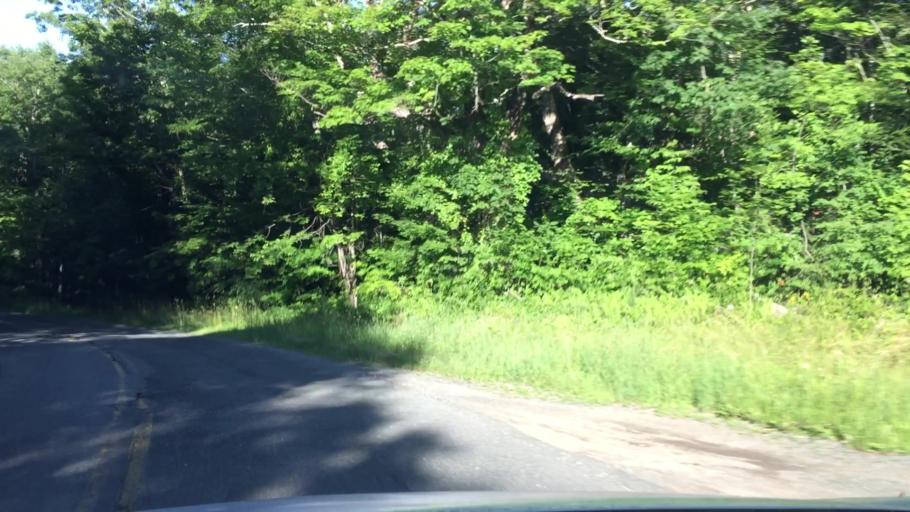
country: US
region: Massachusetts
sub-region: Berkshire County
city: Becket
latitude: 42.3008
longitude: -73.1356
